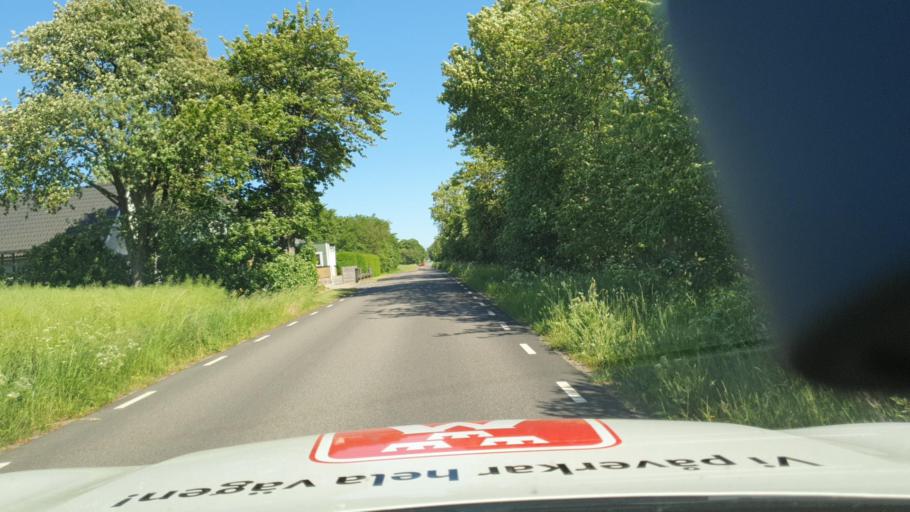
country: SE
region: Skane
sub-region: Sjobo Kommun
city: Sjoebo
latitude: 55.6572
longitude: 13.7123
